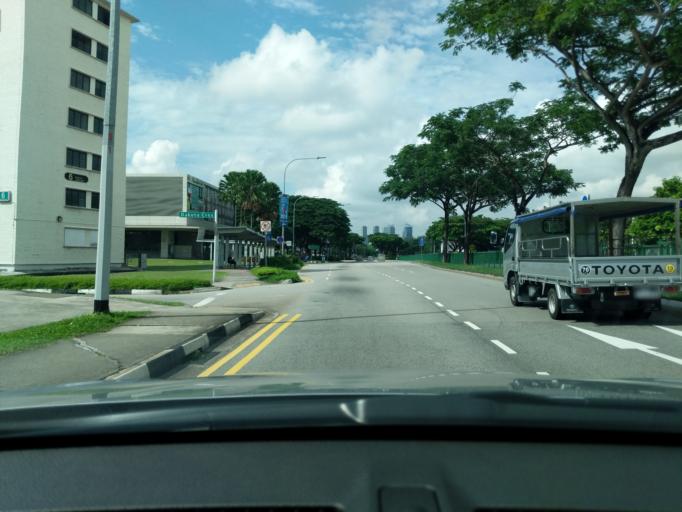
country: SG
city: Singapore
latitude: 1.3067
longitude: 103.8838
